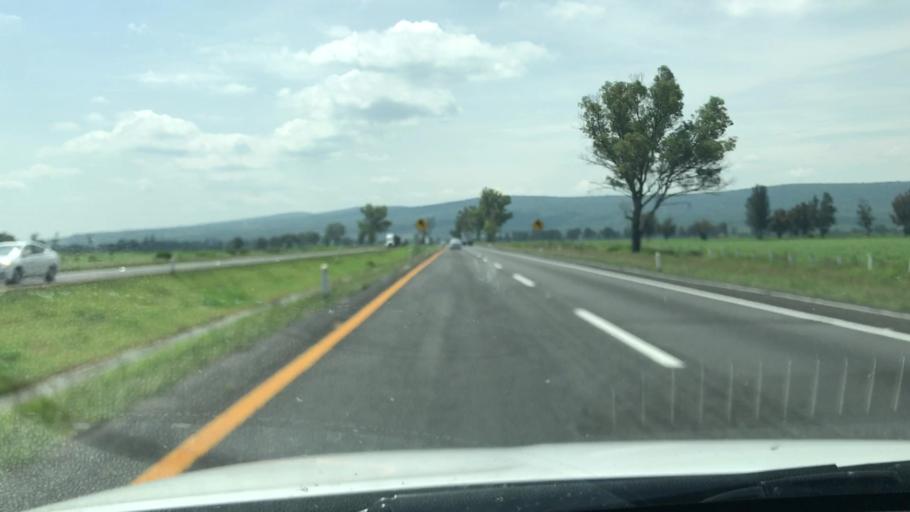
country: MX
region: Jalisco
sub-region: Zapotlan del Rey
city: Zapotlan del Rey
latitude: 20.4541
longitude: -102.8901
